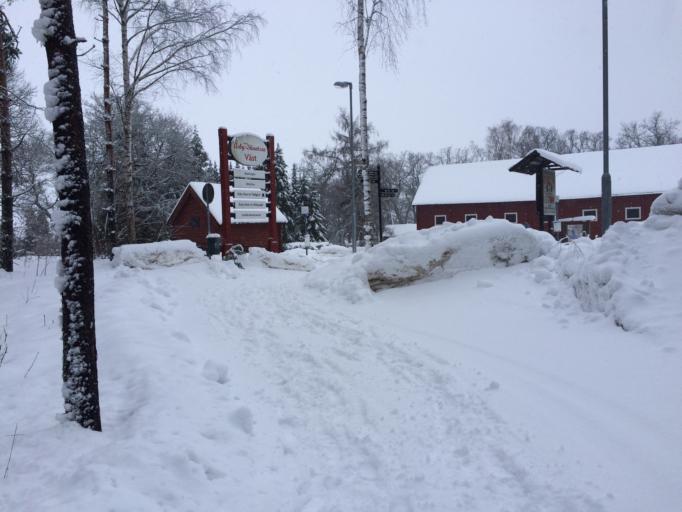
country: SE
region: Vaestmanland
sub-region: Hallstahammars Kommun
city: Hallstahammar
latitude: 59.6125
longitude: 16.2043
